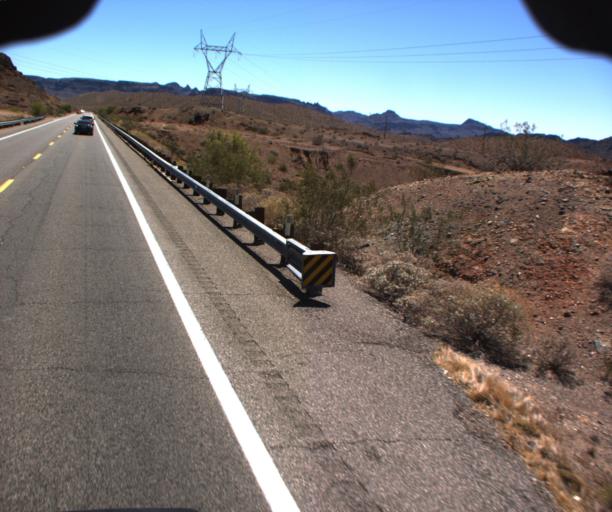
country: US
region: Arizona
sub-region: La Paz County
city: Cienega Springs
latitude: 34.3341
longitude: -114.1374
